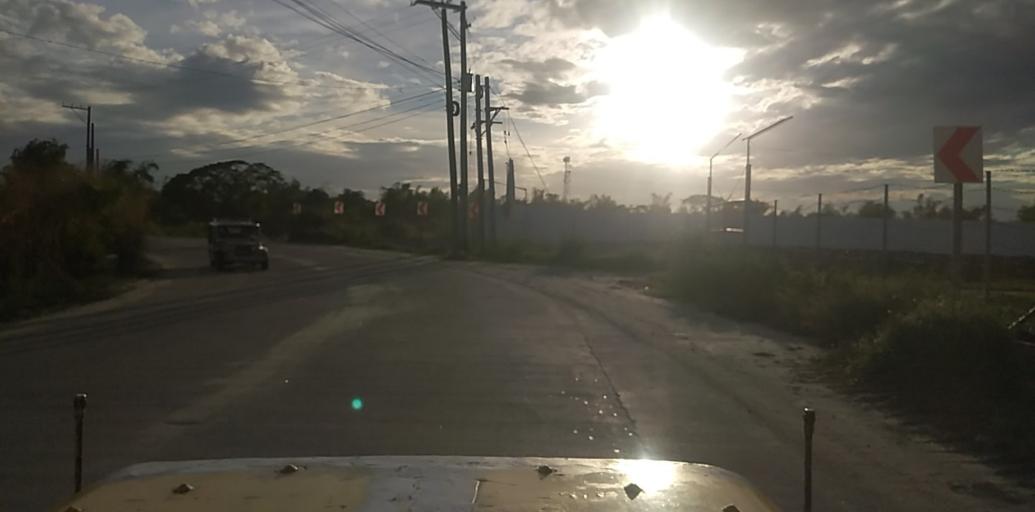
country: PH
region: Central Luzon
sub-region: Province of Pampanga
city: Malino
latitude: 15.1315
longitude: 120.6771
